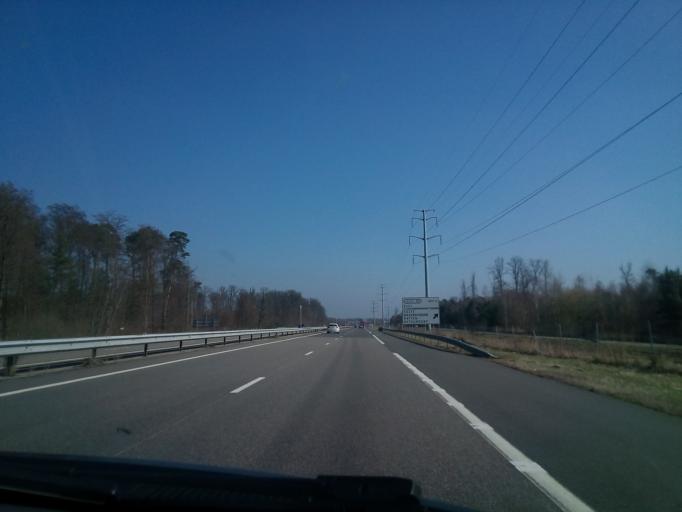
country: FR
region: Alsace
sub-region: Departement du Bas-Rhin
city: Seltz
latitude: 48.8866
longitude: 8.0760
